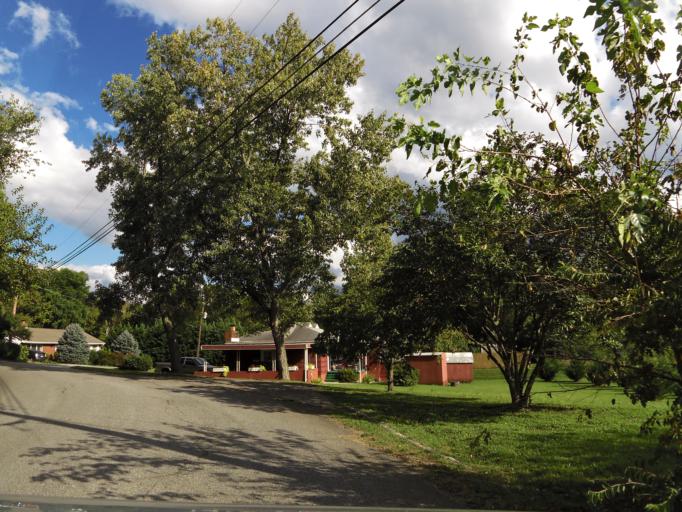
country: US
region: Tennessee
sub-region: Knox County
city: Knoxville
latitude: 36.0025
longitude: -83.9244
